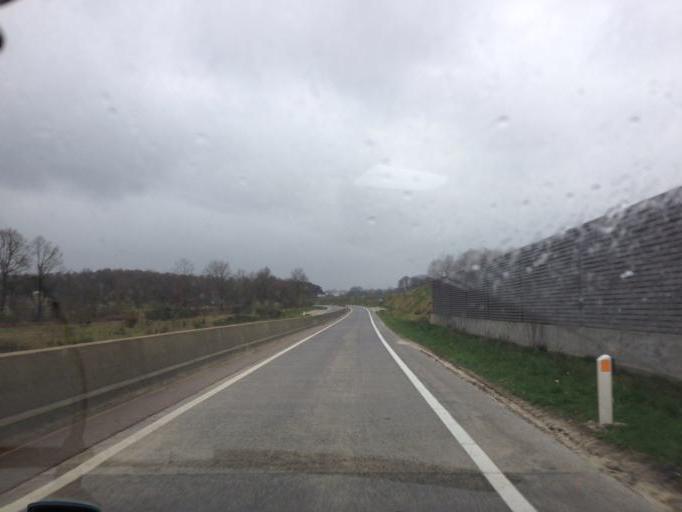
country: BE
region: Flanders
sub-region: Provincie Limburg
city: Opglabbeek
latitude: 51.0936
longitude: 5.5387
